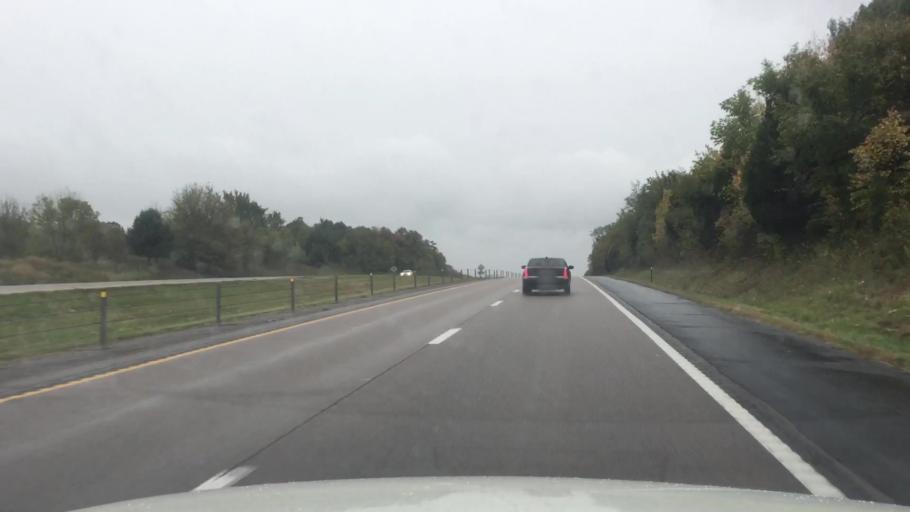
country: US
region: Missouri
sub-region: Boone County
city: Ashland
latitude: 38.6958
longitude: -92.2551
